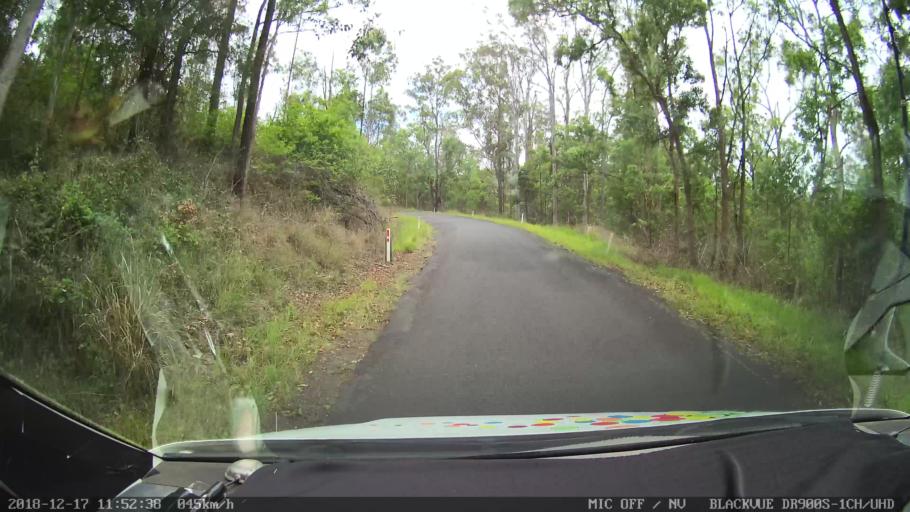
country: AU
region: New South Wales
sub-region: Kyogle
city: Kyogle
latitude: -28.5798
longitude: 152.5886
